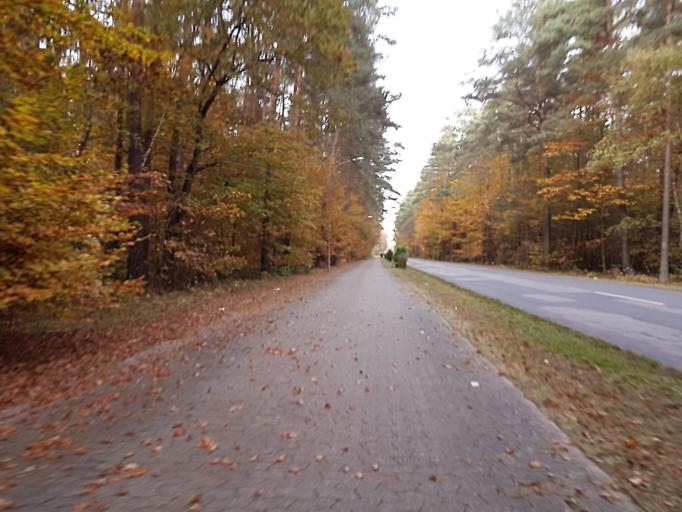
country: DE
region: Bavaria
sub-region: Regierungsbezirk Unterfranken
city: Obernburg am Main
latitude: 49.8187
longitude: 9.1451
